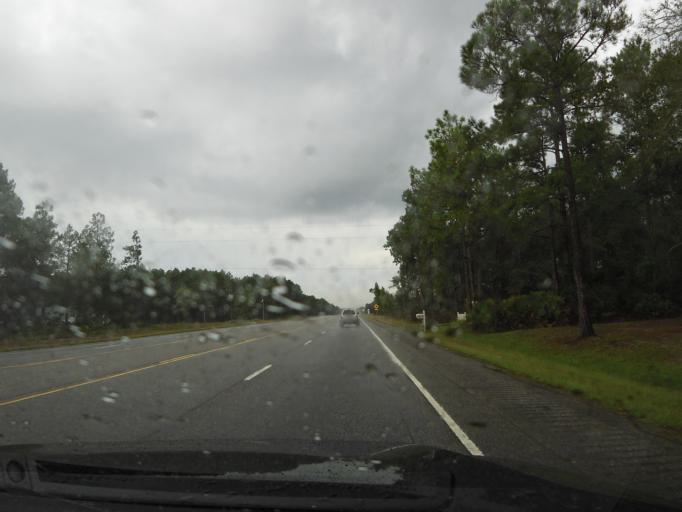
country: US
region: Georgia
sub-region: Wayne County
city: Jesup
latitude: 31.5761
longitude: -81.8476
